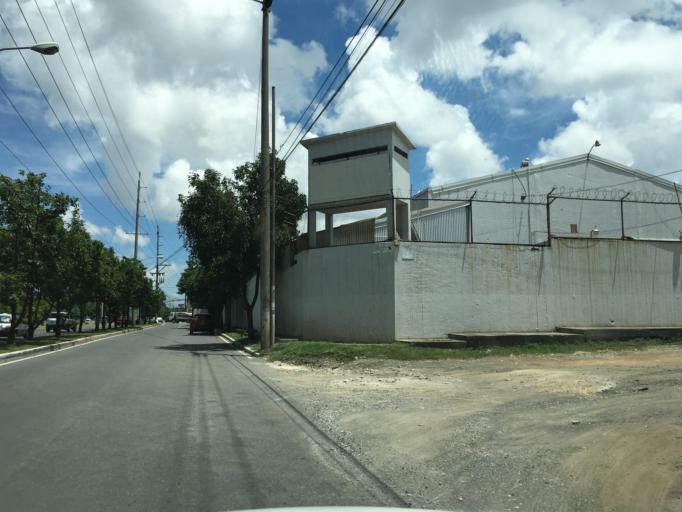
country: GT
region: Guatemala
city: Santa Catarina Pinula
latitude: 14.5905
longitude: -90.5413
